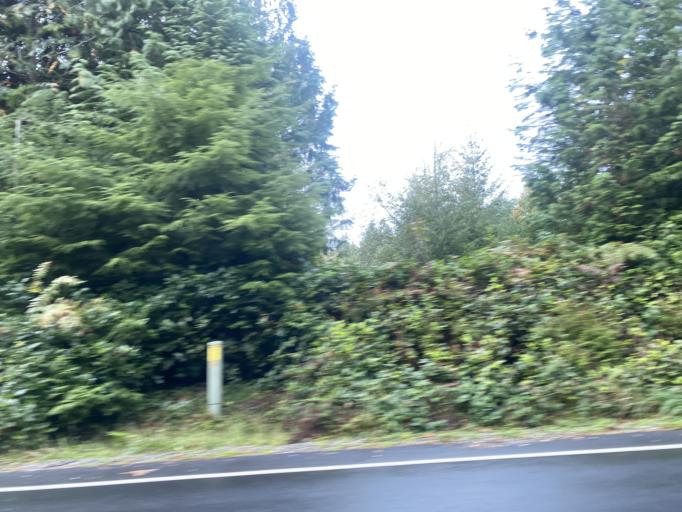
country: US
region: Washington
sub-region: Island County
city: Freeland
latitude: 48.0704
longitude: -122.4850
